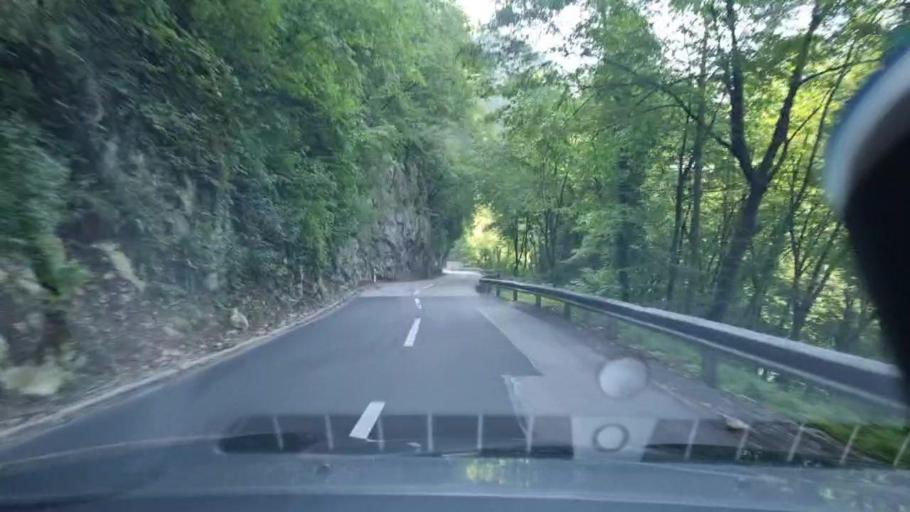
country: BA
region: Federation of Bosnia and Herzegovina
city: Stijena
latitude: 44.8832
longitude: 16.0631
